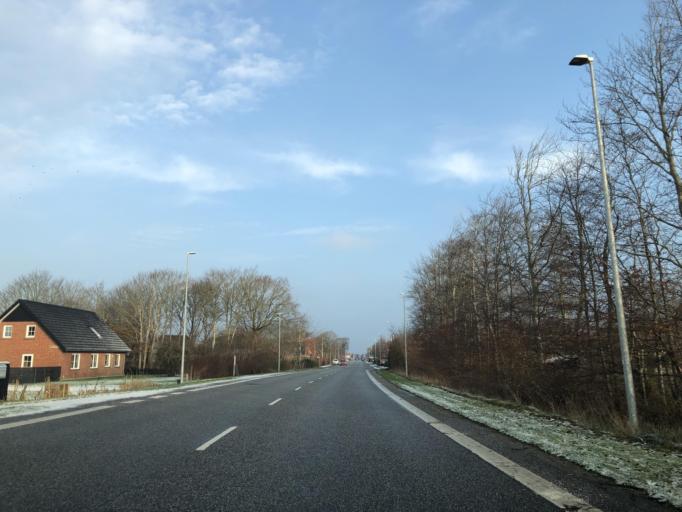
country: DK
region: Central Jutland
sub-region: Ringkobing-Skjern Kommune
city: Tarm
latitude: 55.8985
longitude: 8.5148
